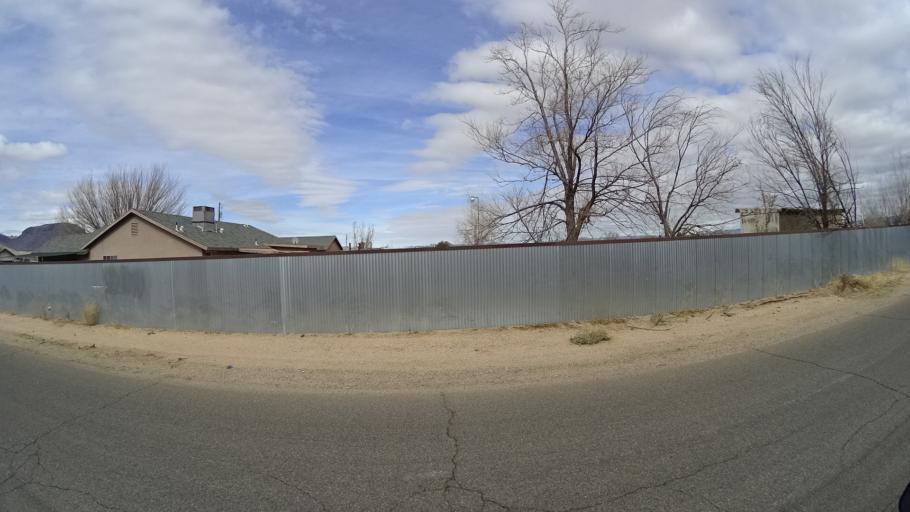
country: US
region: Arizona
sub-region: Mohave County
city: New Kingman-Butler
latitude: 35.2321
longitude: -114.0092
